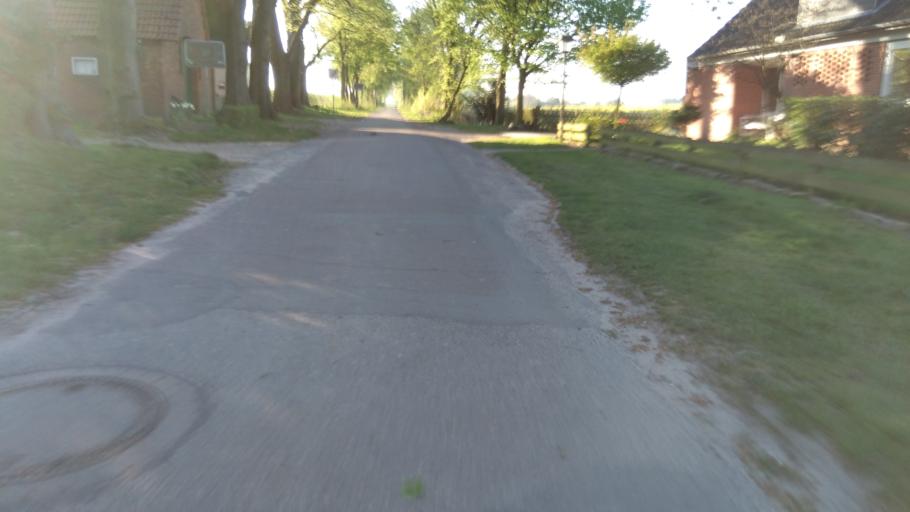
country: DE
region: Lower Saxony
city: Bliedersdorf
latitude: 53.4787
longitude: 9.5737
